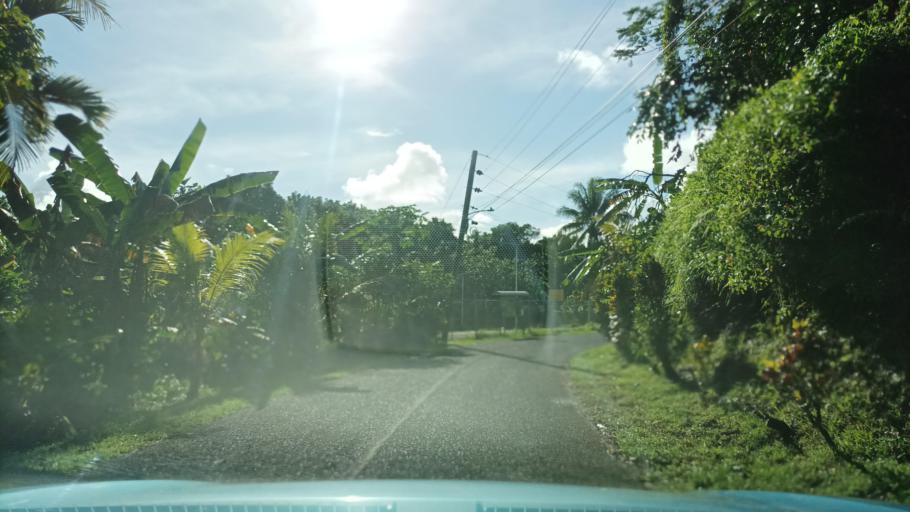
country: FM
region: Pohnpei
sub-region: Kolonia Municipality
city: Kolonia Town
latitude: 6.9552
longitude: 158.1898
